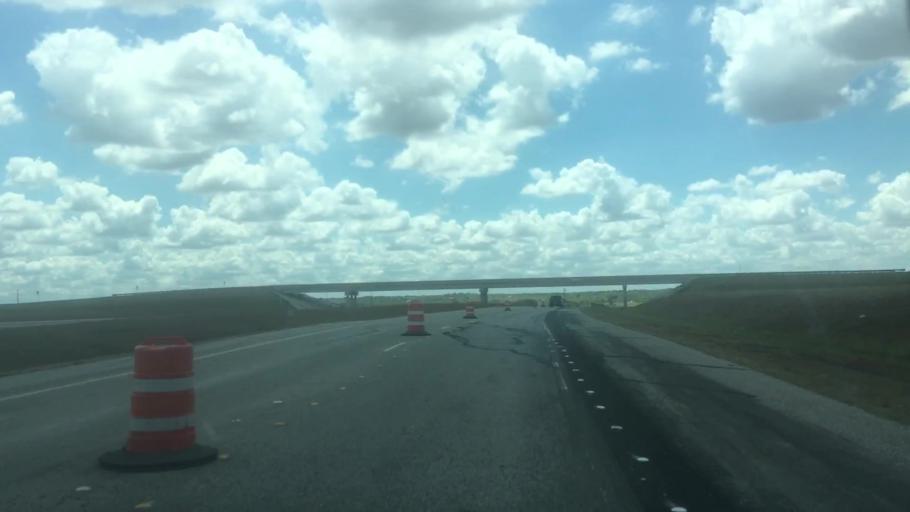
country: US
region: Texas
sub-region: Caldwell County
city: Lockhart
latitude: 29.8384
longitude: -97.7313
